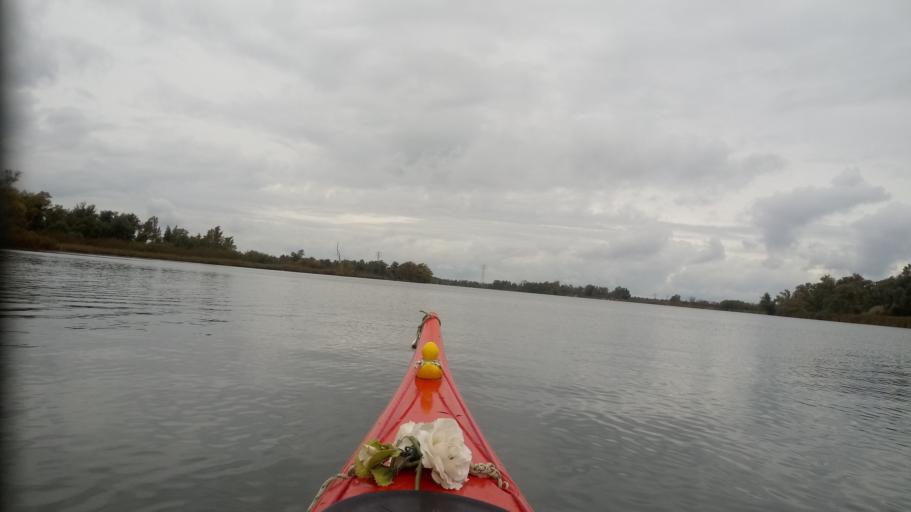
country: NL
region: North Brabant
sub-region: Gemeente Made en Drimmelen
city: Drimmelen
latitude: 51.7538
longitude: 4.8227
